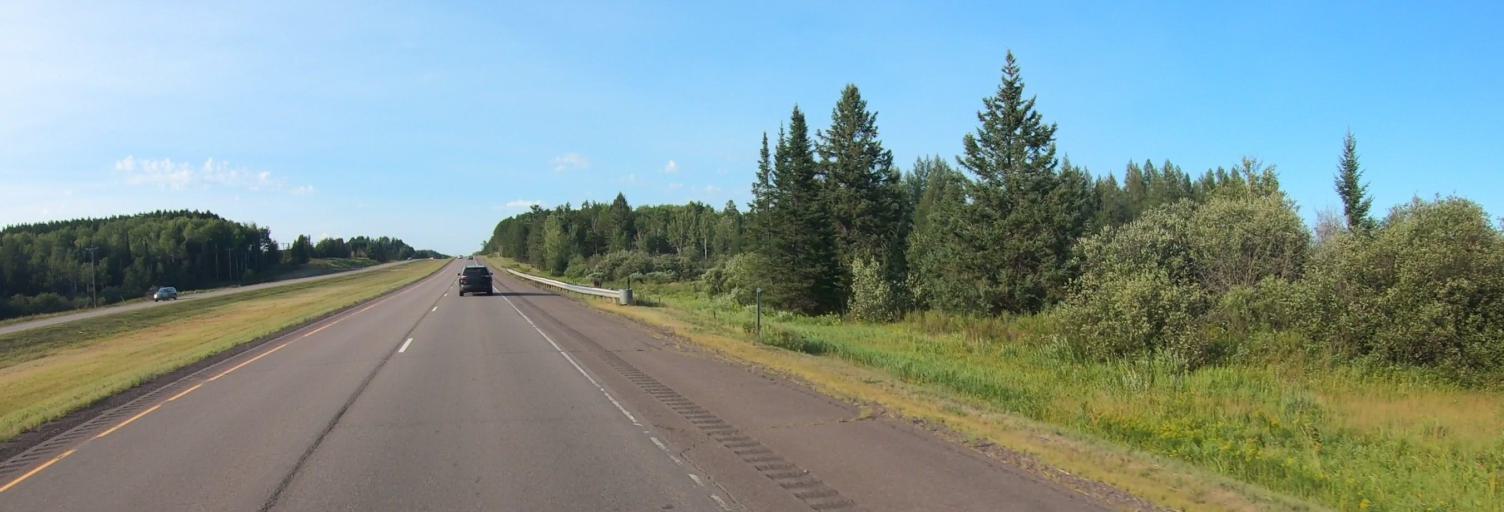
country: US
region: Minnesota
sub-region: Carlton County
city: Cloquet
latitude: 46.9844
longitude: -92.4707
